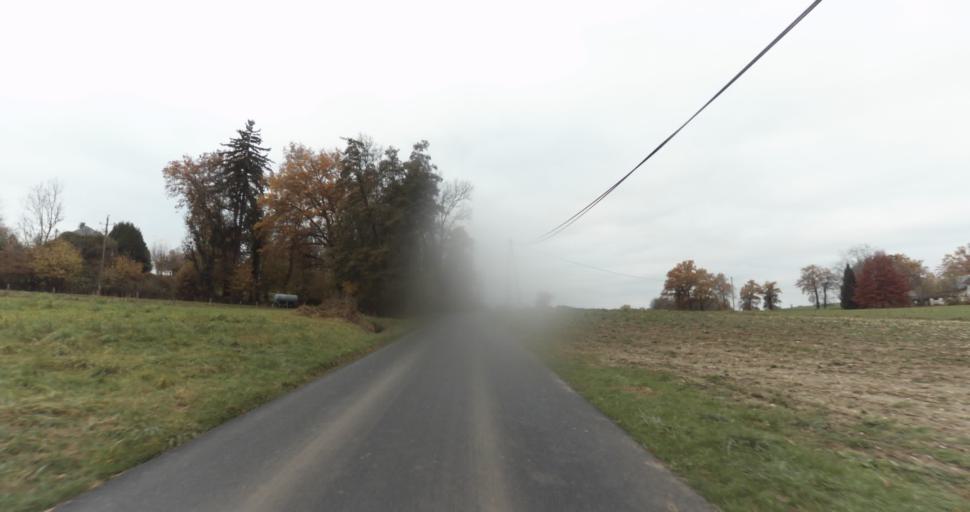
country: FR
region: Rhone-Alpes
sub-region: Departement de la Savoie
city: Albens
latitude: 45.7527
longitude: 5.9753
